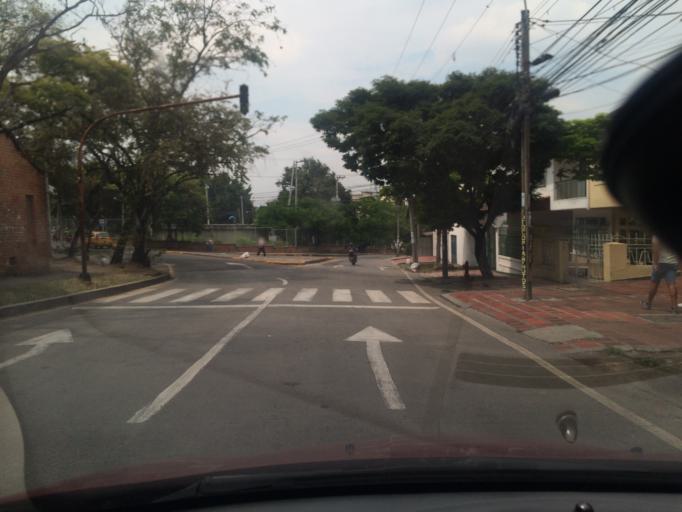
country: CO
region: Valle del Cauca
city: Cali
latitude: 3.4288
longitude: -76.5472
